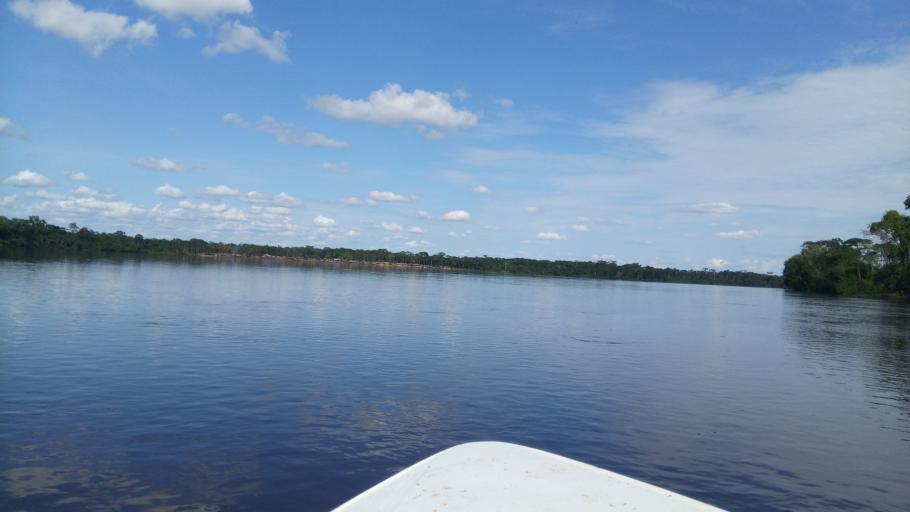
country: CD
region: Eastern Province
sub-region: Sous-Region de la Tshopo
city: Yangambi
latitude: 0.5525
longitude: 24.2409
